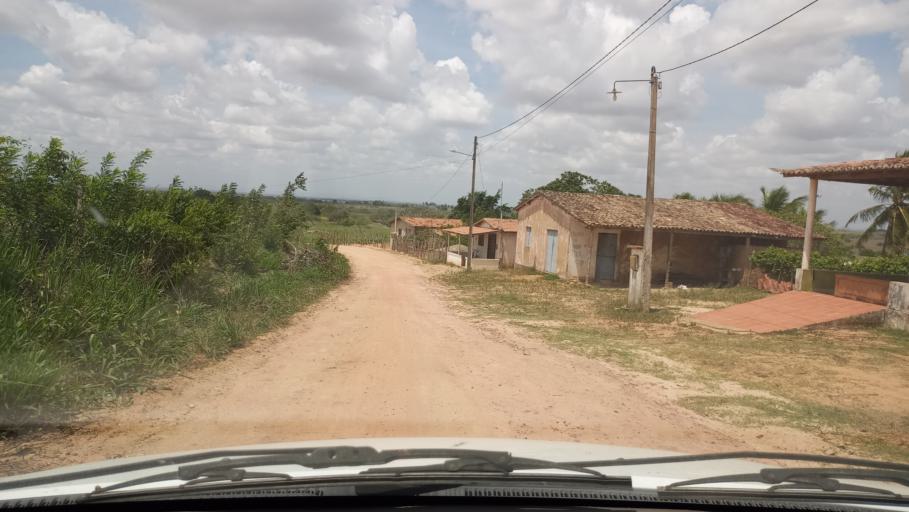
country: BR
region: Rio Grande do Norte
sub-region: Brejinho
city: Brejinho
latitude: -6.2652
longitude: -35.3430
